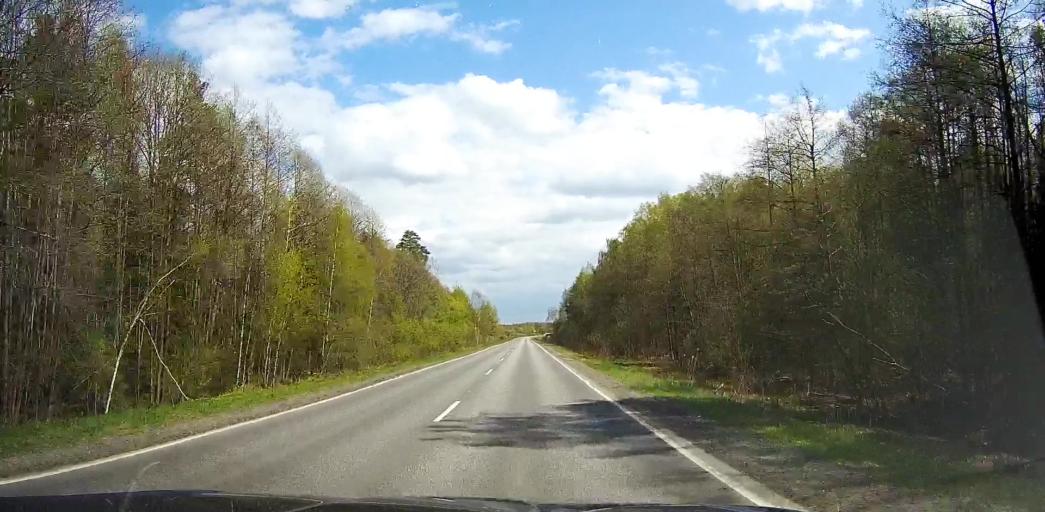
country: RU
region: Moskovskaya
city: Davydovo
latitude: 55.5513
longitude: 38.7845
